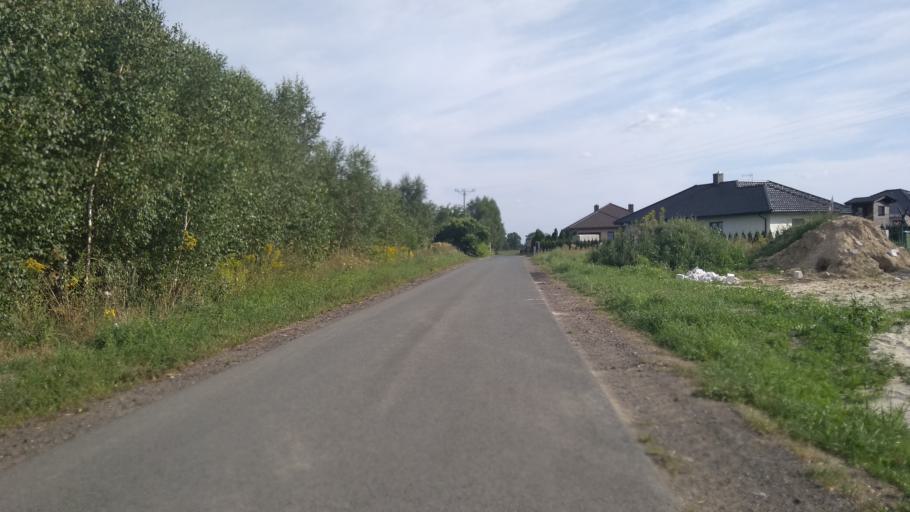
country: PL
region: Kujawsko-Pomorskie
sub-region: Powiat bydgoski
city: Osielsko
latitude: 53.2201
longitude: 18.1460
